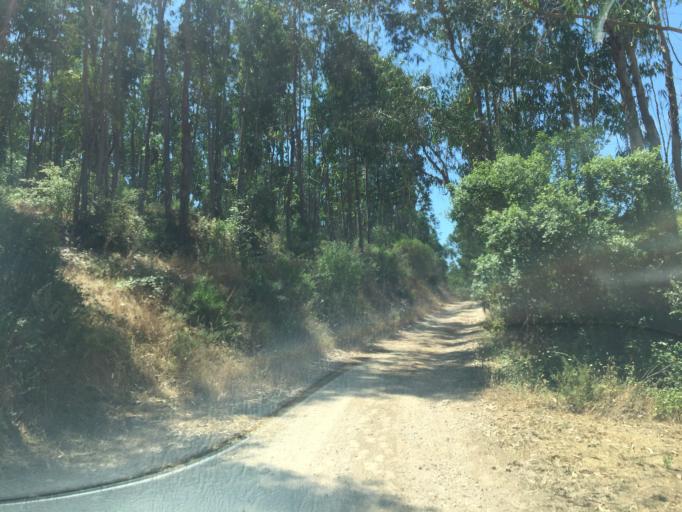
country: PT
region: Santarem
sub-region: Tomar
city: Tomar
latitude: 39.6057
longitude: -8.3587
